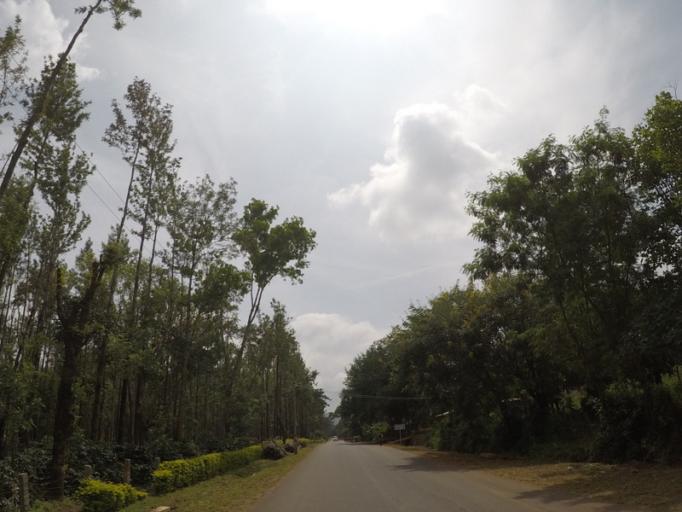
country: IN
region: Karnataka
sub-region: Chikmagalur
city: Chikmagalur
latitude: 13.4152
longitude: 75.7993
